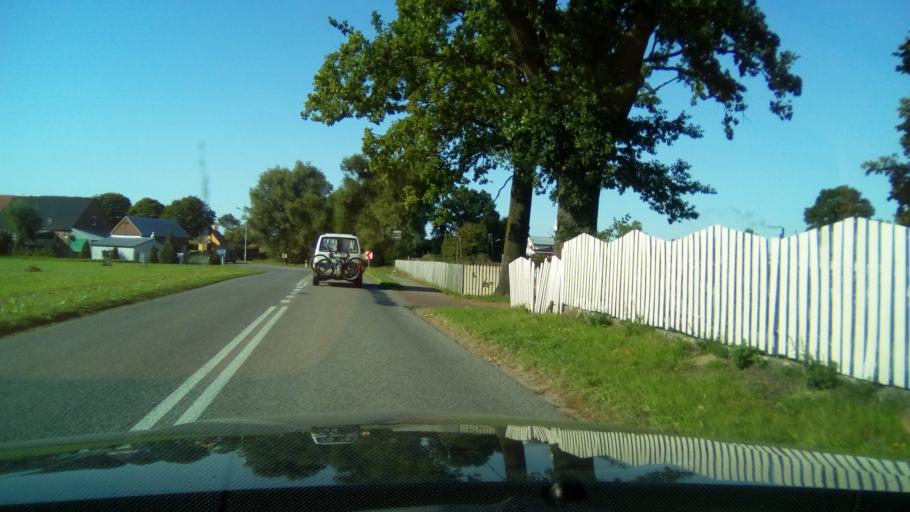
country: PL
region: West Pomeranian Voivodeship
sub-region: Powiat kamienski
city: Golczewo
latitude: 53.8312
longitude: 14.9262
